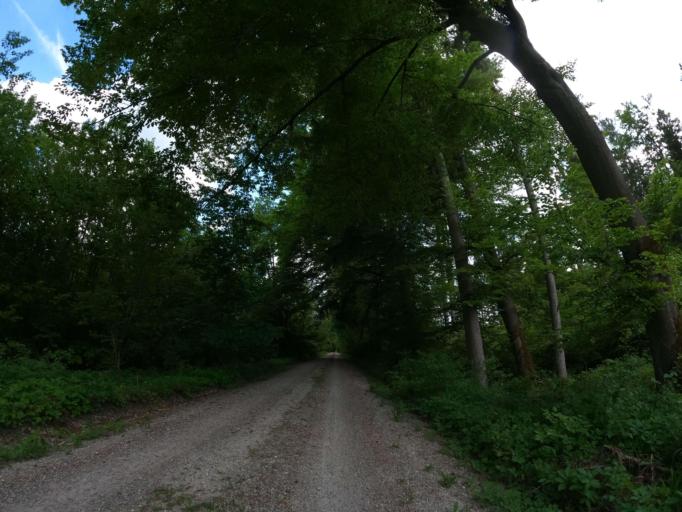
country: DE
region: Bavaria
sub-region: Upper Bavaria
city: Brunnthal
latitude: 47.9769
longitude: 11.6920
